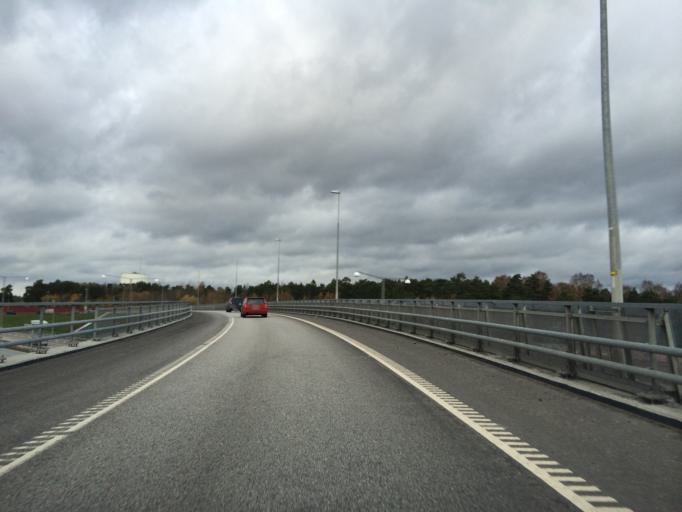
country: SE
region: Stockholm
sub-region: Stockholms Kommun
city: Kista
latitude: 59.4034
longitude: 17.9690
